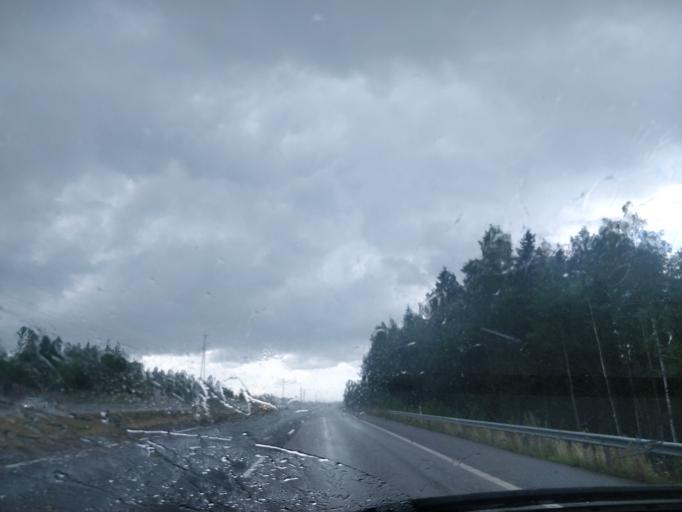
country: FI
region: Uusimaa
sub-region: Helsinki
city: Kerava
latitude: 60.4116
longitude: 25.1257
